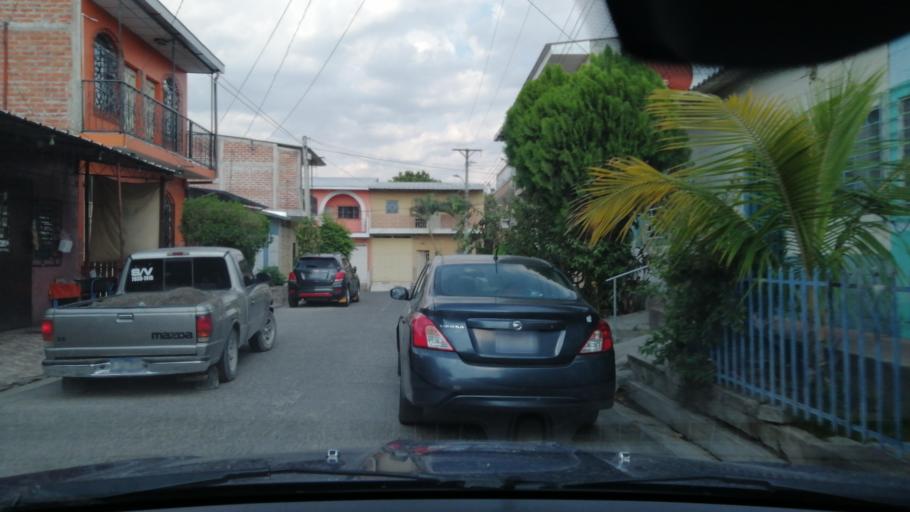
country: SV
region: Santa Ana
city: Metapan
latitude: 14.3295
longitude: -89.4373
